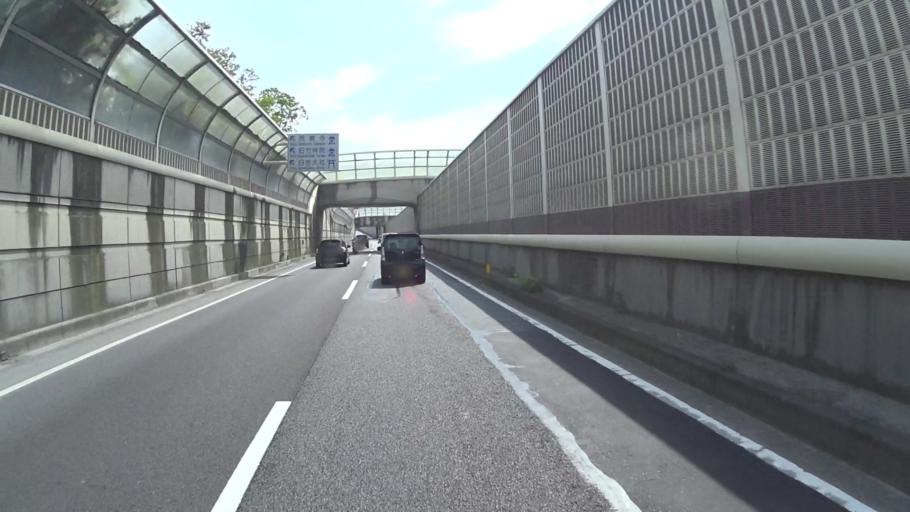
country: JP
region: Shiga Prefecture
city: Otsu-shi
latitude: 35.0512
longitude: 135.8633
